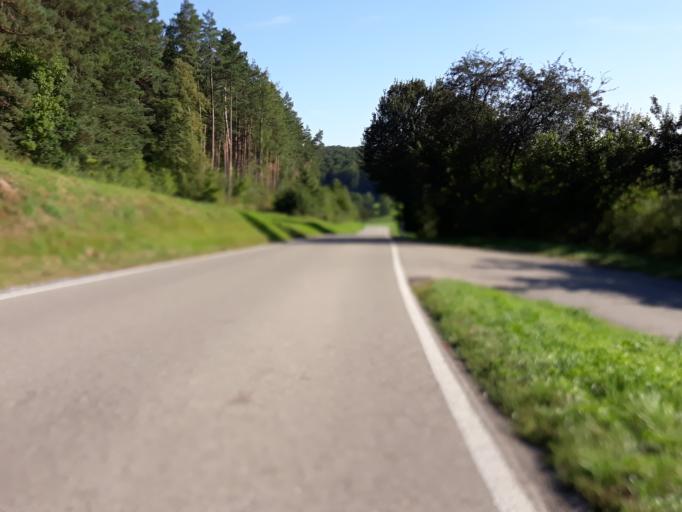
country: DE
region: Baden-Wuerttemberg
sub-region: Karlsruhe Region
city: Gechingen
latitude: 48.7046
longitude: 8.8389
